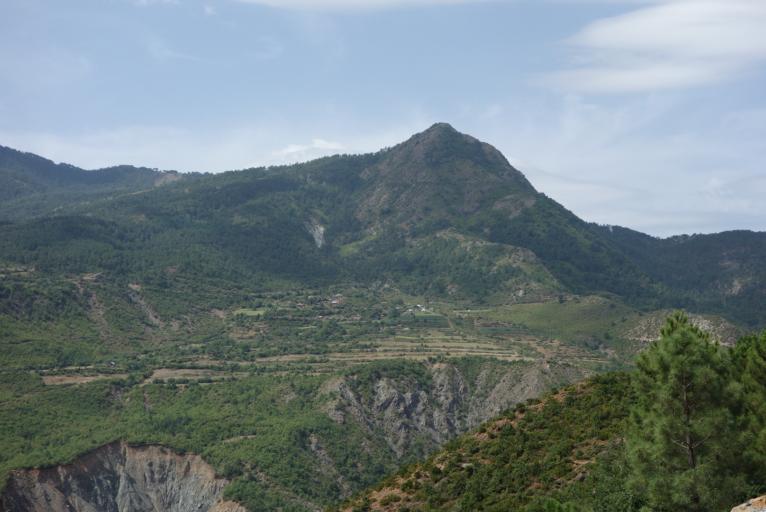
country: AL
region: Elbasan
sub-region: Rrethi i Gramshit
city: Kodovjat
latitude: 40.7734
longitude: 20.3070
